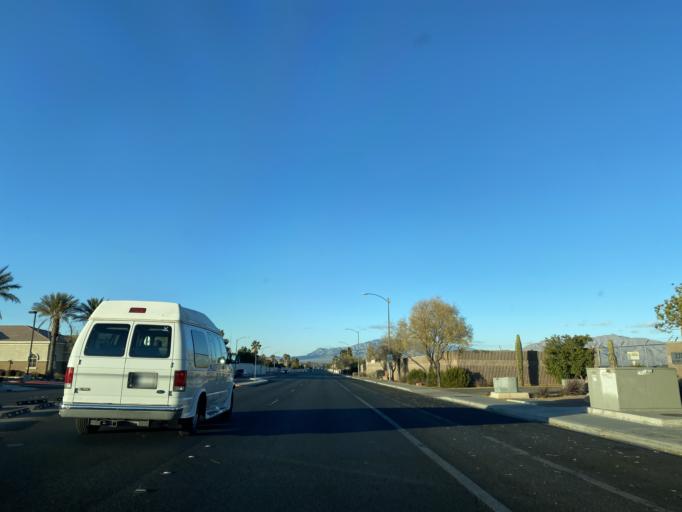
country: US
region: Nevada
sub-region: Clark County
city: Summerlin South
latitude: 36.2193
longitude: -115.2971
